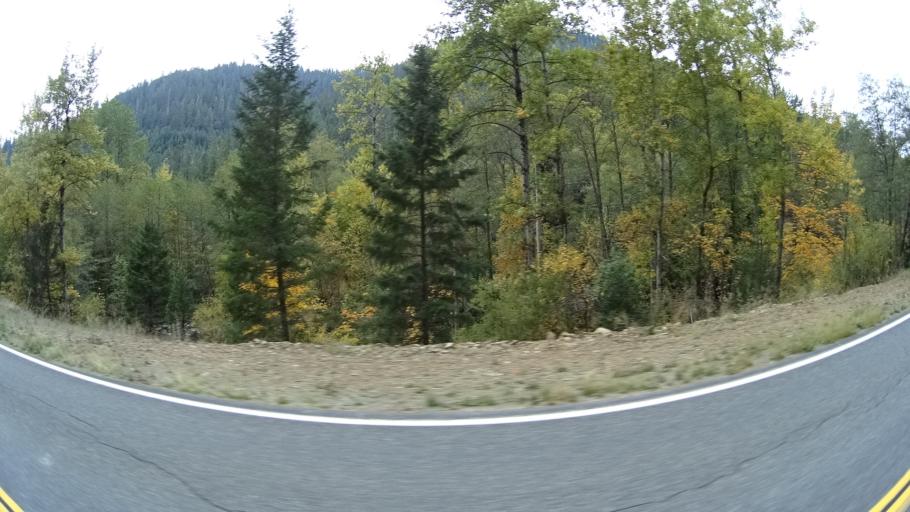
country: US
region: California
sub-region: Siskiyou County
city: Happy Camp
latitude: 41.8904
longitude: -123.4328
